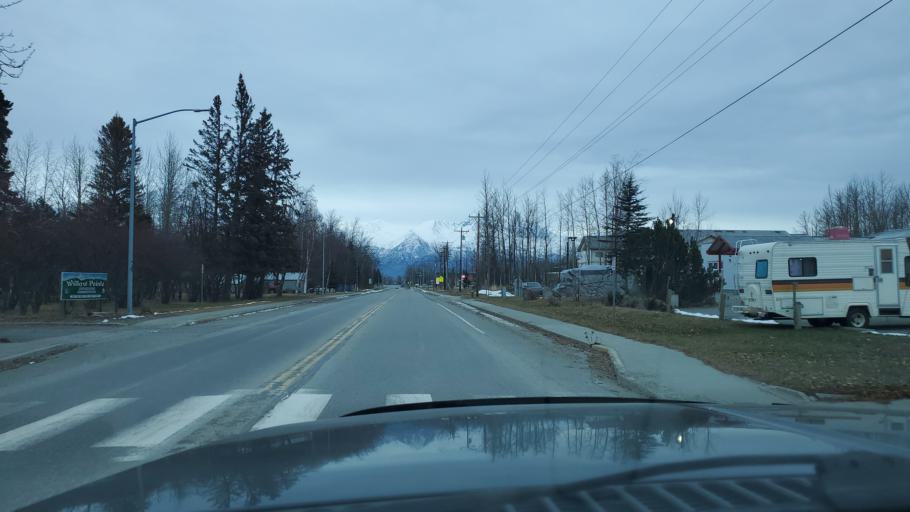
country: US
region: Alaska
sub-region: Matanuska-Susitna Borough
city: Palmer
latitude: 61.5967
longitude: -149.1108
